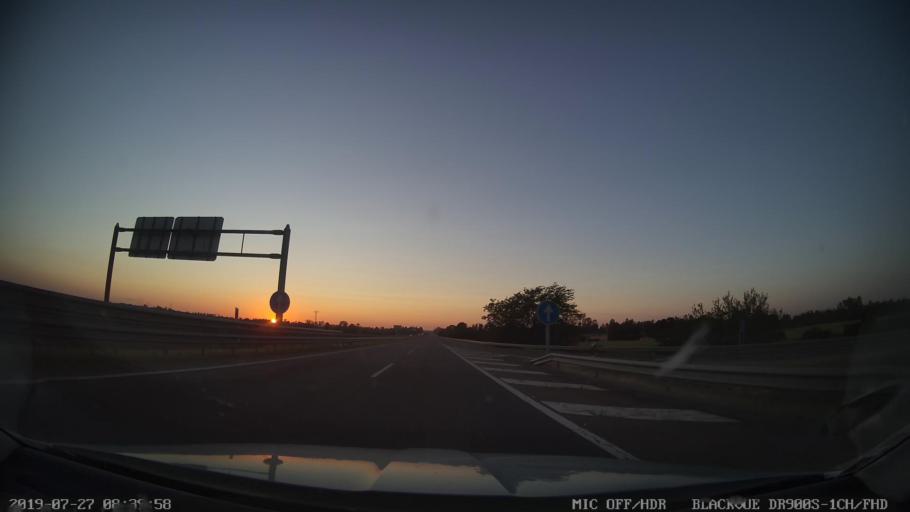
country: ES
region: Extremadura
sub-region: Provincia de Badajoz
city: Badajoz
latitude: 38.8910
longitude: -6.9161
